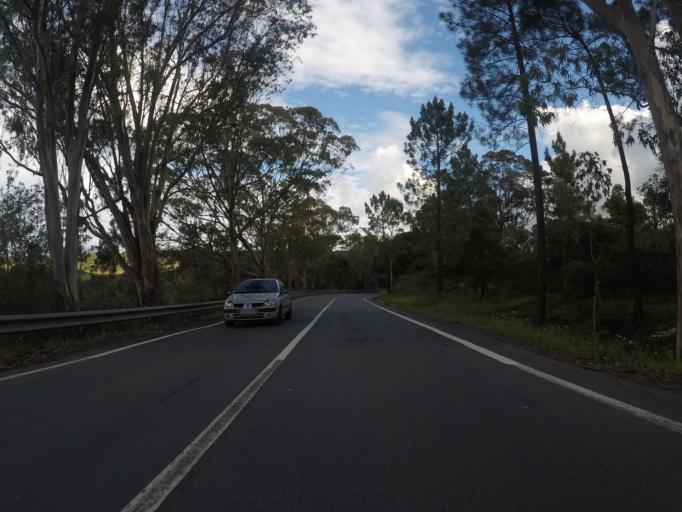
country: PT
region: Faro
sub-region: Aljezur
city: Aljezur
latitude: 37.2522
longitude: -8.8108
